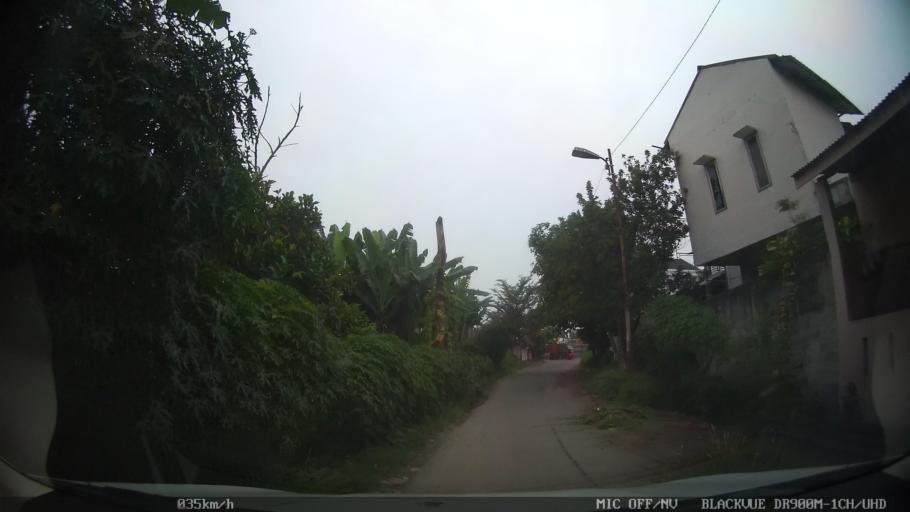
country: ID
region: North Sumatra
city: Deli Tua
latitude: 3.5483
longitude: 98.7150
